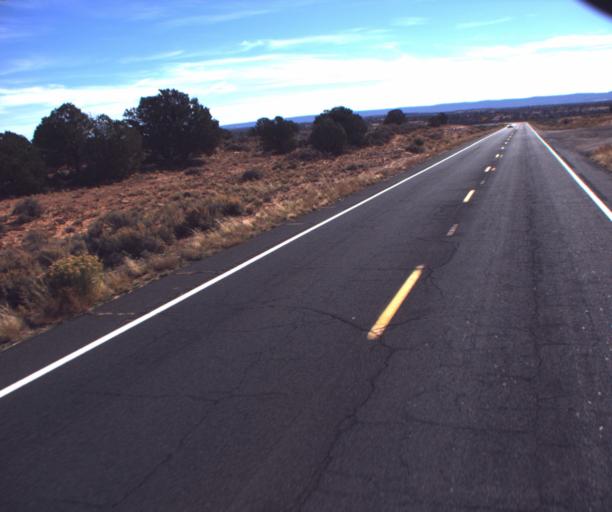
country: US
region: Arizona
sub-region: Coconino County
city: Kaibito
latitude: 36.5635
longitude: -110.7551
